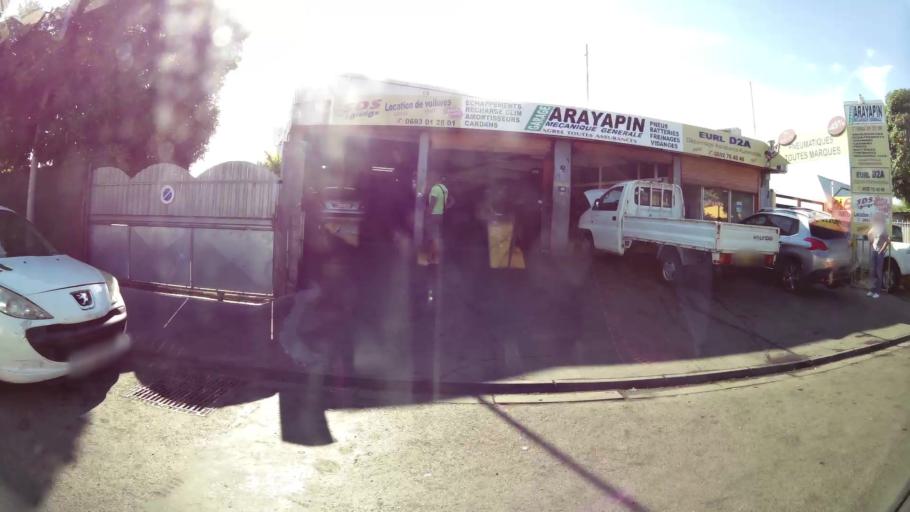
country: RE
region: Reunion
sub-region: Reunion
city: Saint-Louis
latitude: -21.2903
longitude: 55.4139
